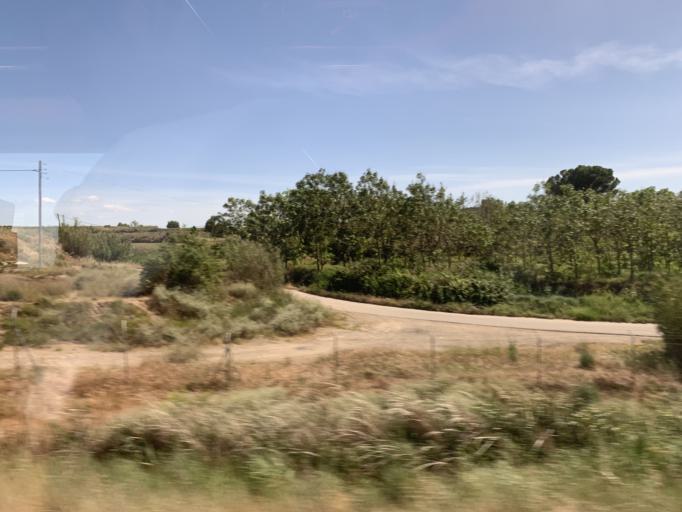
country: ES
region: Catalonia
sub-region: Provincia de Lleida
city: Aspa
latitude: 41.5644
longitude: 0.6993
